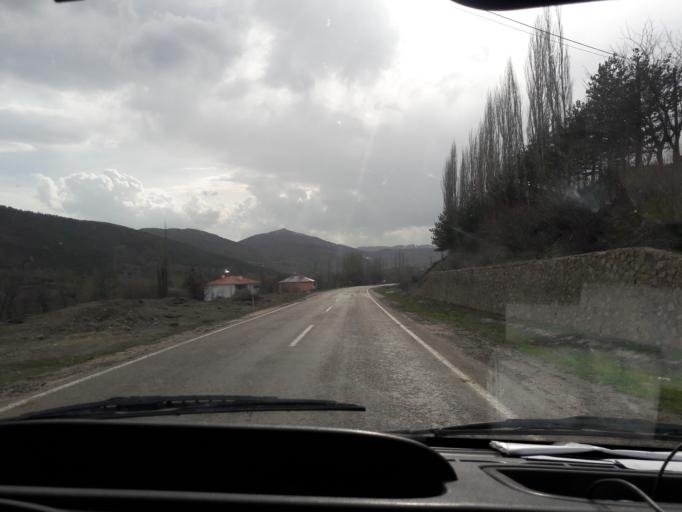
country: TR
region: Giresun
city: Alucra
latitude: 40.2643
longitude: 38.9166
